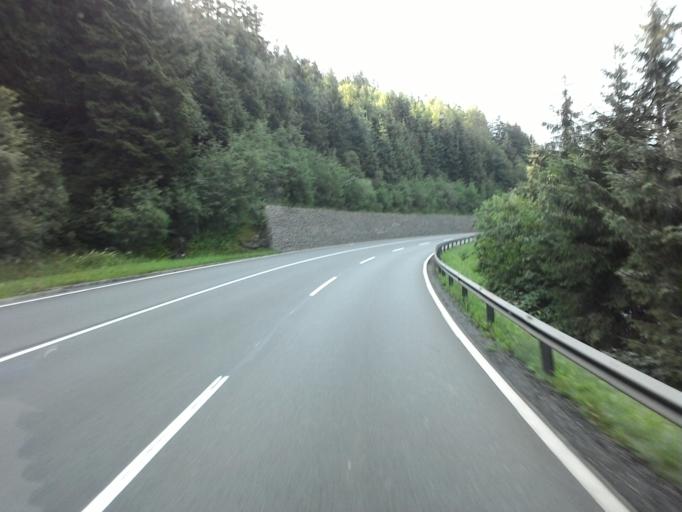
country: AT
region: Salzburg
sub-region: Politischer Bezirk Zell am See
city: Mittersill
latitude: 47.2510
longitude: 12.4883
